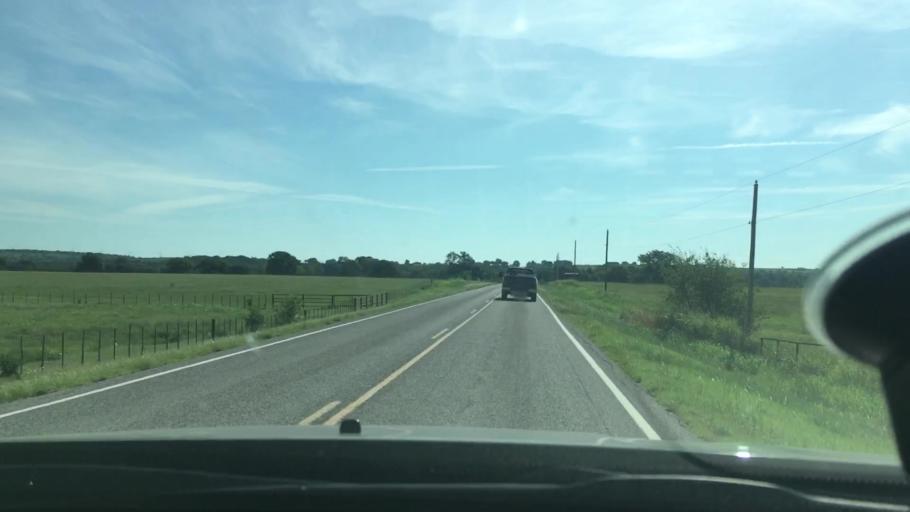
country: US
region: Oklahoma
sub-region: Carter County
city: Lone Grove
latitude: 34.3327
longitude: -97.2418
